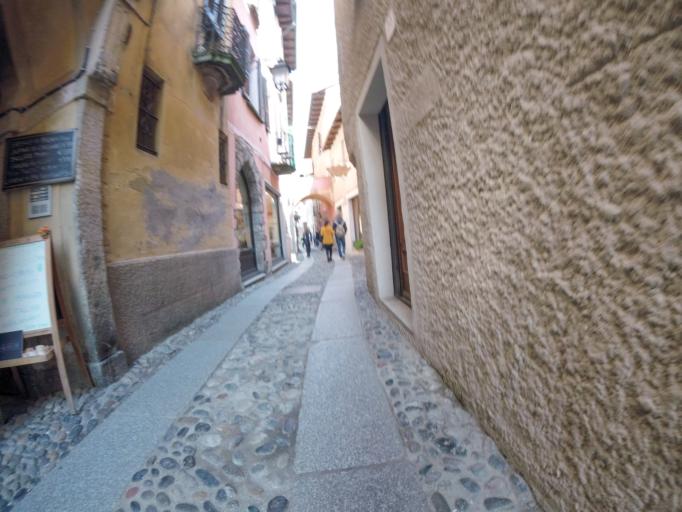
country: IT
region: Piedmont
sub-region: Provincia di Novara
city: Orta San Giulio
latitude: 45.7992
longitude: 8.4058
